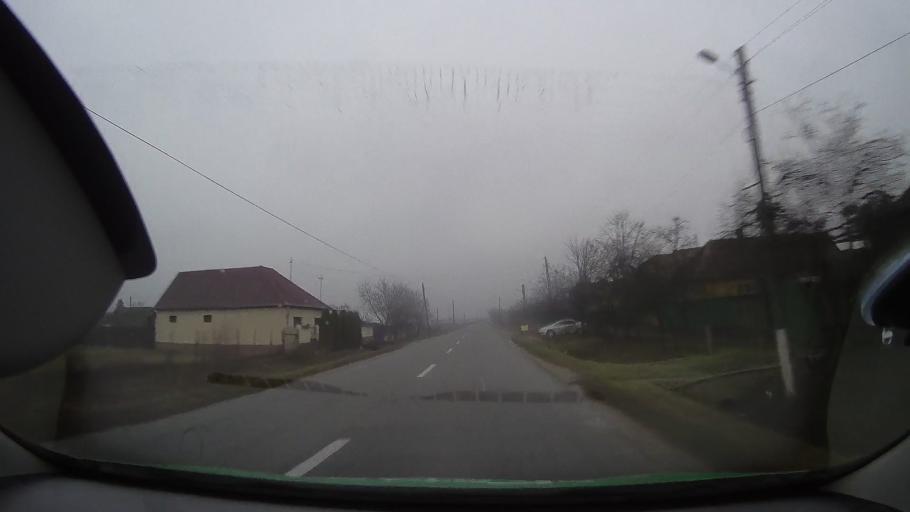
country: RO
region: Bihor
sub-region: Comuna Tulca
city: Tulca
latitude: 46.7936
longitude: 21.7466
